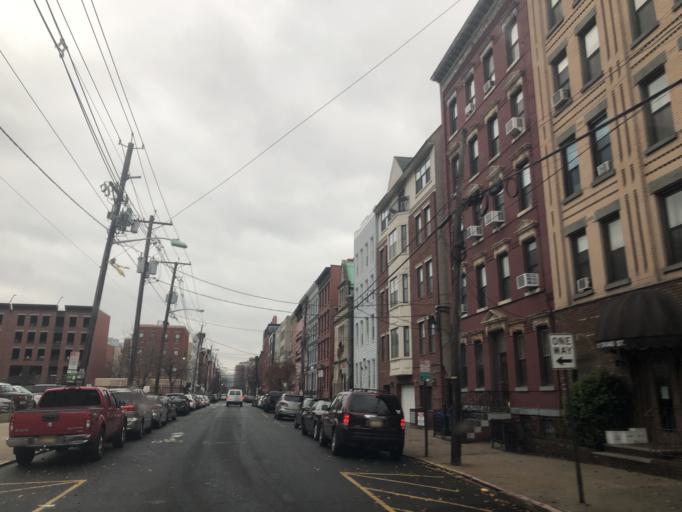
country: US
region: New Jersey
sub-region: Hudson County
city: Hoboken
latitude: 40.7431
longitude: -74.0349
